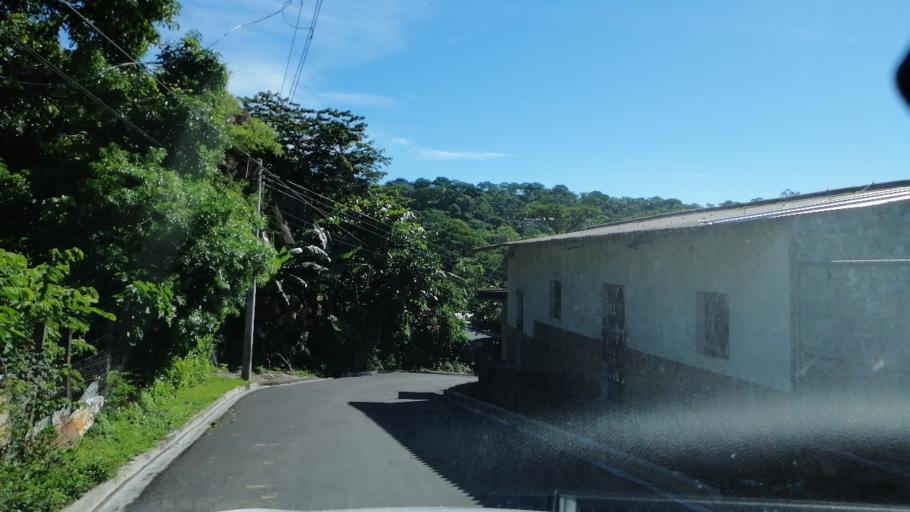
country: SV
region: Morazan
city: Corinto
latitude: 13.8097
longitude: -87.9766
